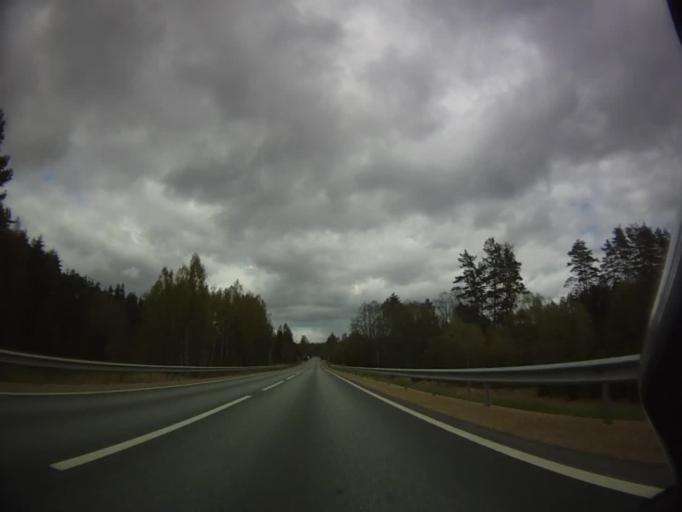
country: LV
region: Ligatne
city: Ligatne
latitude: 57.2913
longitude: 24.9184
